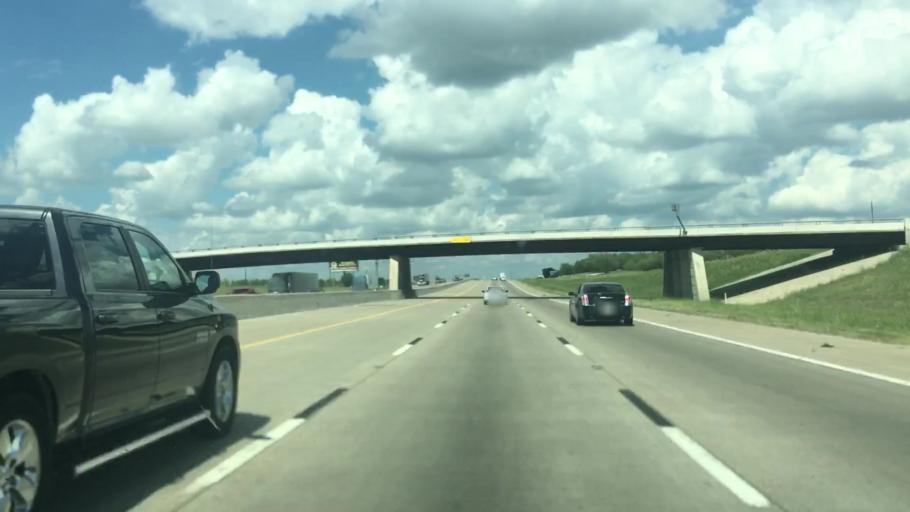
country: US
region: Texas
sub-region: Hill County
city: Hillsboro
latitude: 31.9727
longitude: -97.1168
